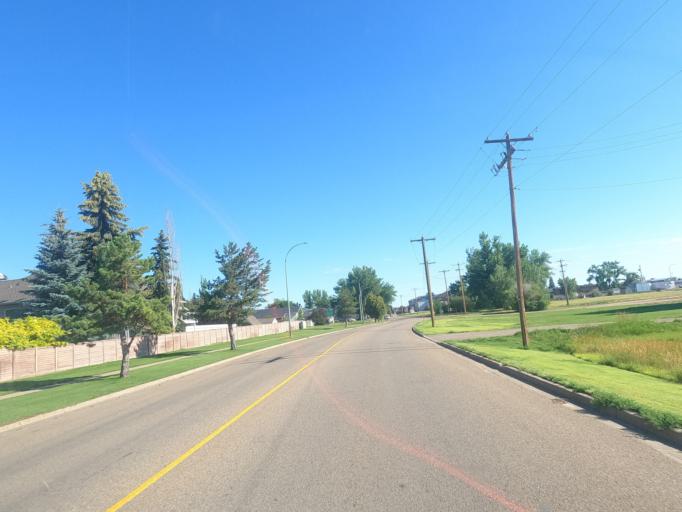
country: CA
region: Alberta
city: Brooks
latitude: 50.5803
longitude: -111.9000
